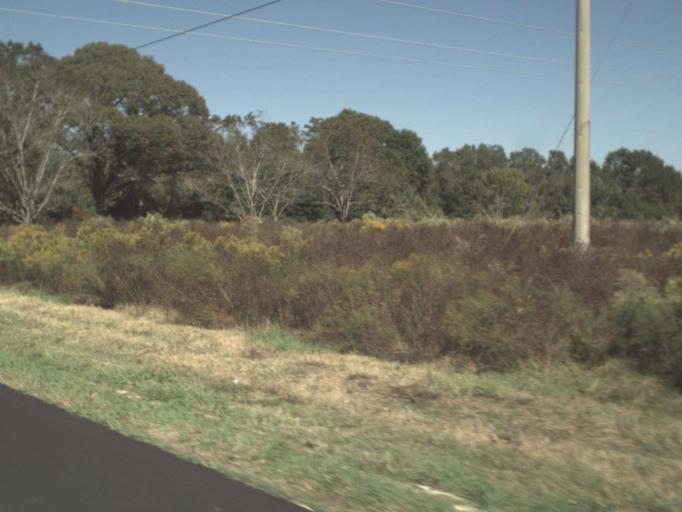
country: US
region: Alabama
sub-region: Covington County
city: Florala
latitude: 30.8548
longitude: -86.2466
